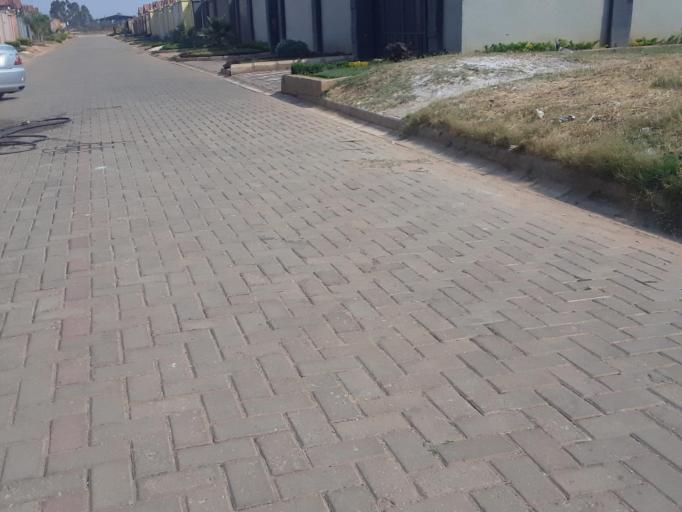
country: ZM
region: Lusaka
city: Lusaka
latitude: -15.3614
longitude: 28.2851
